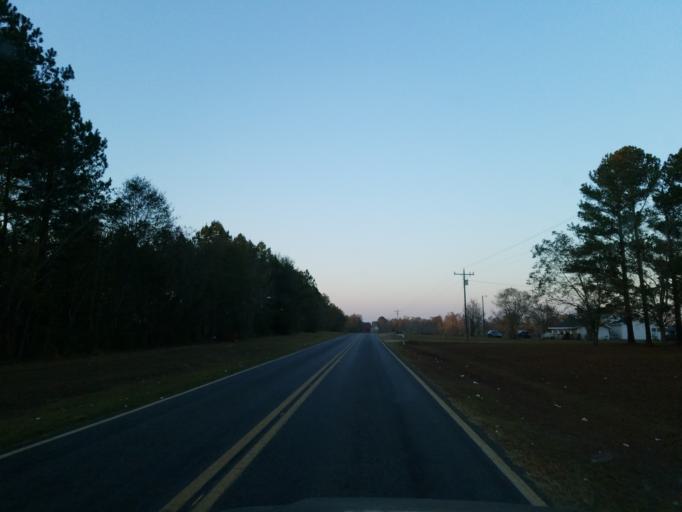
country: US
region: Georgia
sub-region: Ben Hill County
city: Fitzgerald
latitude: 31.7081
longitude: -83.3850
